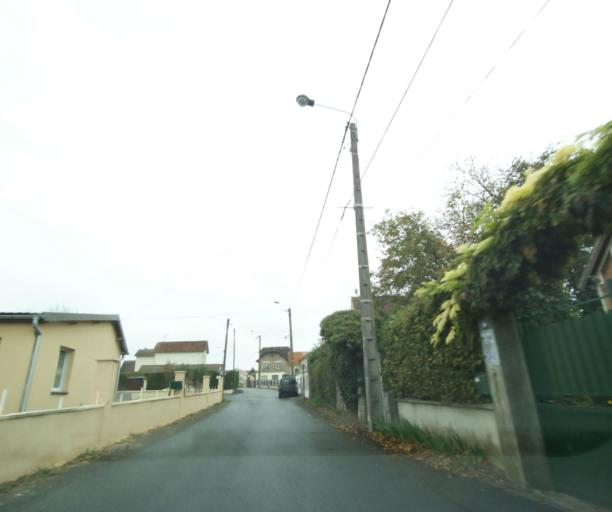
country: FR
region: Centre
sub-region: Departement d'Eure-et-Loir
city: Dreux
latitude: 48.7266
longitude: 1.3641
